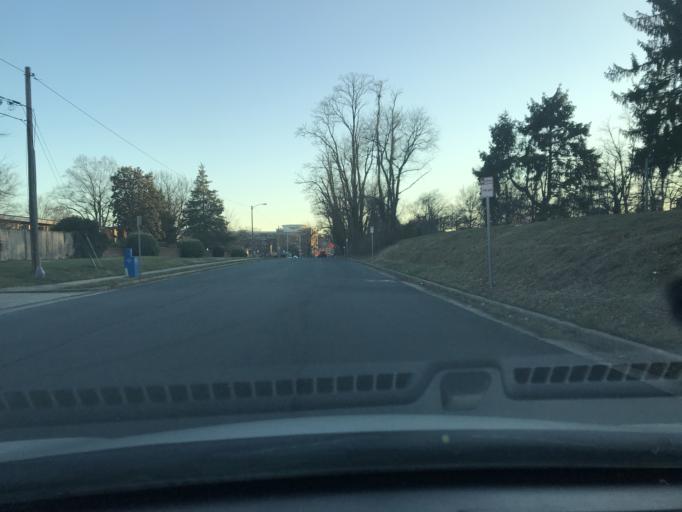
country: US
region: Virginia
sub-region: City of Fairfax
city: Fairfax
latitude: 38.8630
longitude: -77.3071
